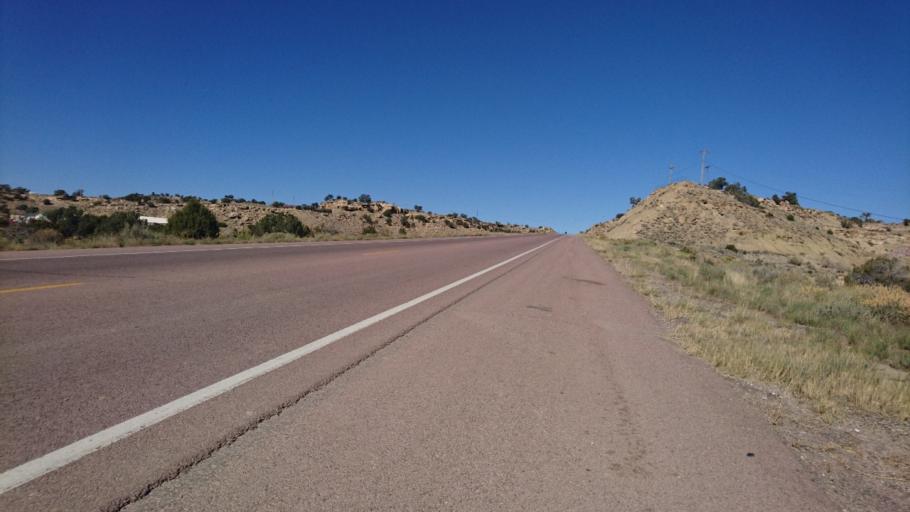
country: US
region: New Mexico
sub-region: McKinley County
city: Gallup
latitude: 35.4717
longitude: -108.7423
